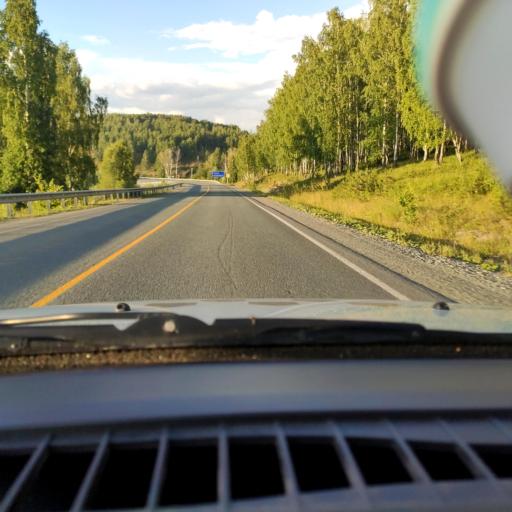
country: RU
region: Chelyabinsk
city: Karabash
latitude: 55.3389
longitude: 60.2410
